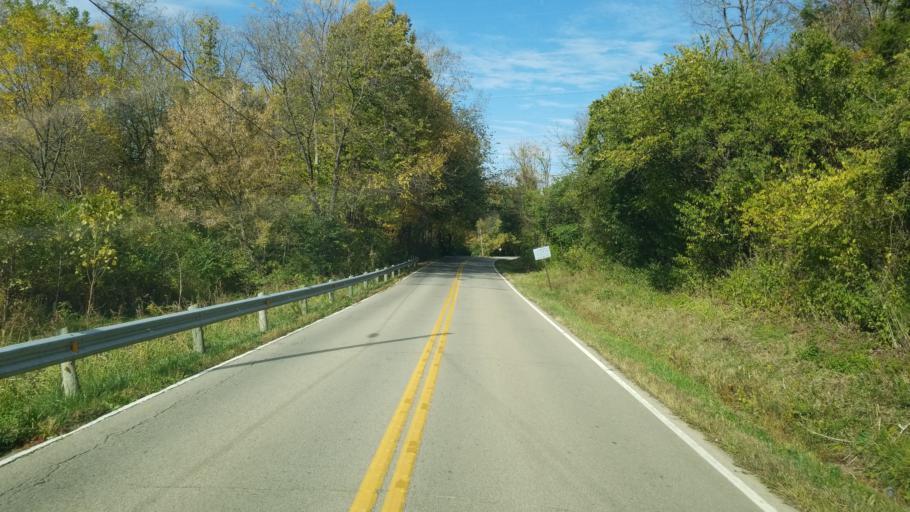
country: US
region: Ohio
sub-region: Warren County
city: Morrow
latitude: 39.3620
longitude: -84.1422
